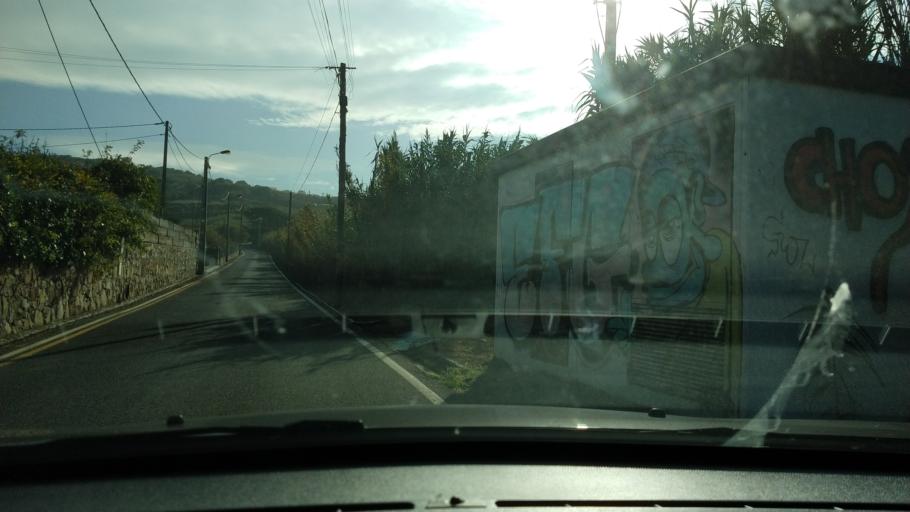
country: PT
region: Lisbon
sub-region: Sintra
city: Colares
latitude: 38.7986
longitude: -9.4832
